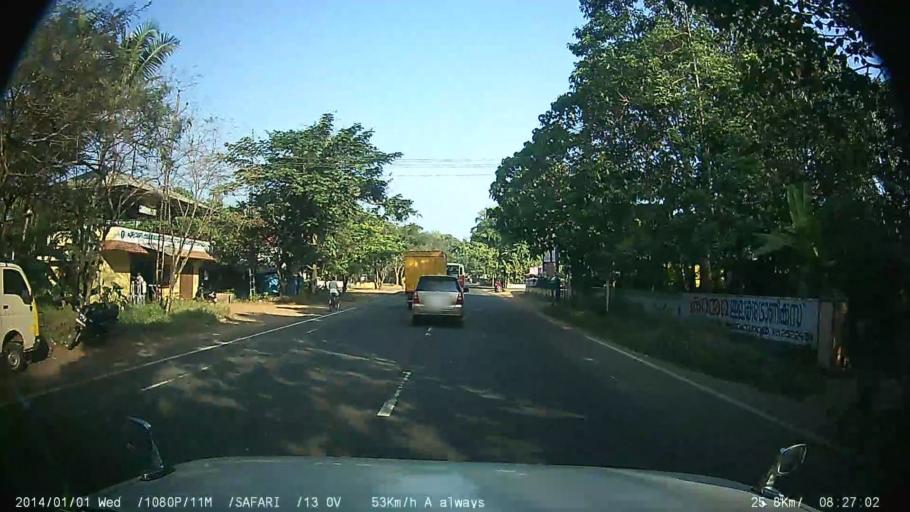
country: IN
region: Kerala
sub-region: Ernakulam
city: Perumbavoor
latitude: 10.0817
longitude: 76.5033
